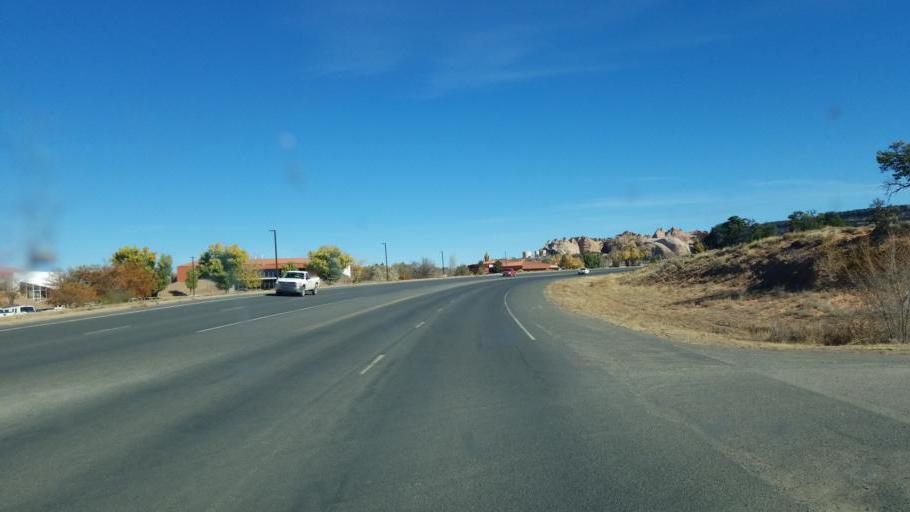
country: US
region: Arizona
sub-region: Apache County
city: Window Rock
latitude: 35.6736
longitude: -109.0564
